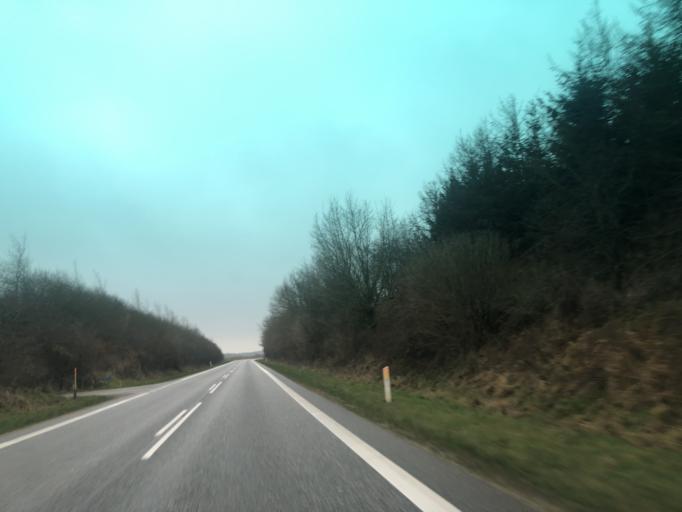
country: DK
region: North Denmark
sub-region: Thisted Kommune
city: Hurup
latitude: 56.7370
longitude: 8.4347
